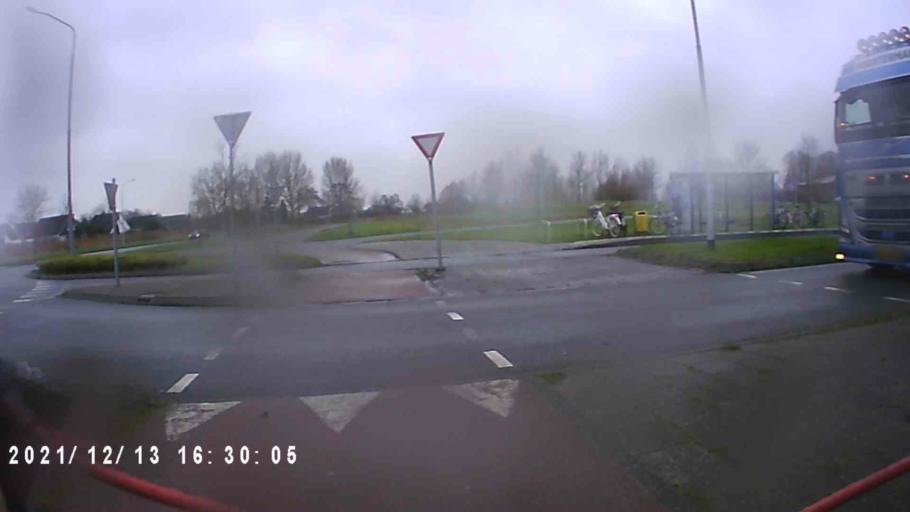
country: NL
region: Groningen
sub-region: Gemeente Appingedam
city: Appingedam
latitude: 53.3222
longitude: 6.8884
